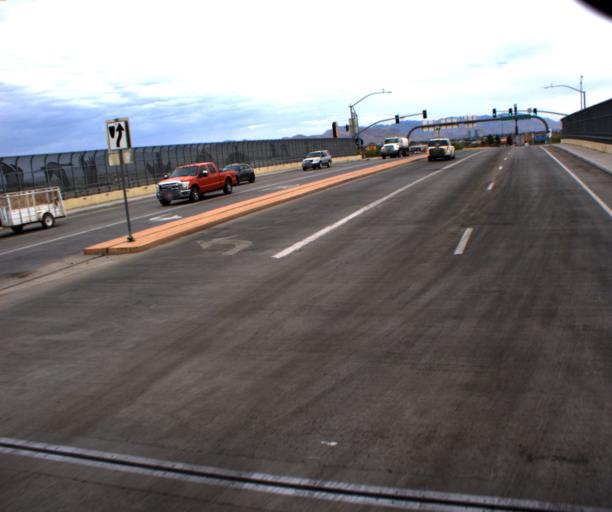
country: US
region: Arizona
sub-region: Cochise County
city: Willcox
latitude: 32.2663
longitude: -109.8434
